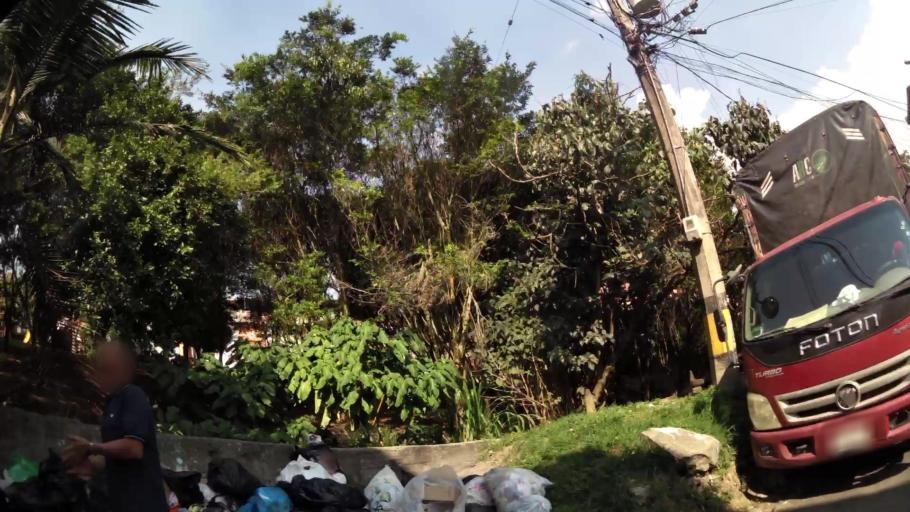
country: CO
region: Antioquia
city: Medellin
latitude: 6.2919
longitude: -75.5928
